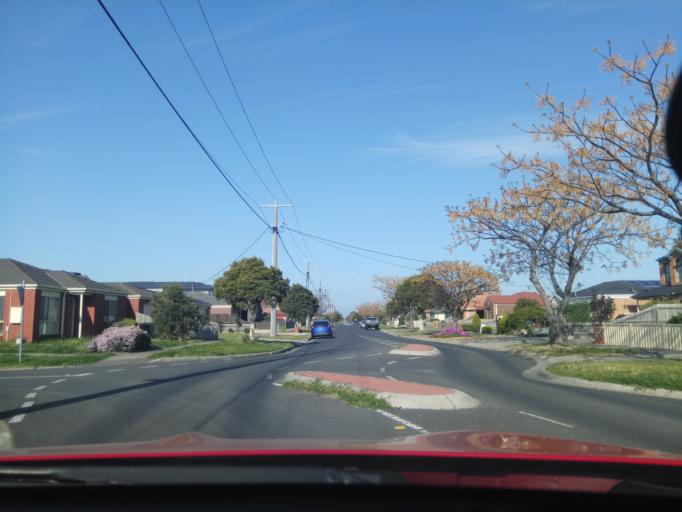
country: AU
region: Victoria
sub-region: Hobsons Bay
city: Altona Meadows
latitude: -37.8794
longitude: 144.7718
